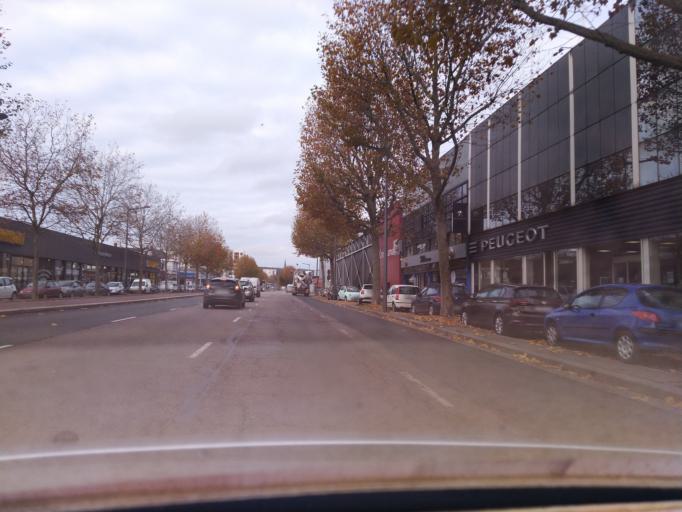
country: FR
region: Haute-Normandie
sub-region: Departement de la Seine-Maritime
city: Rouen
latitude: 49.4455
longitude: 1.0728
